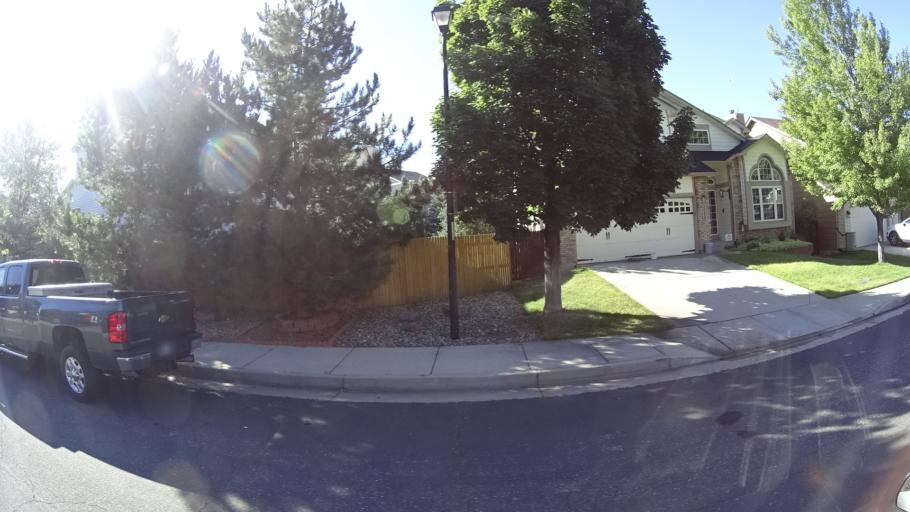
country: US
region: Colorado
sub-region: El Paso County
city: Black Forest
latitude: 38.9604
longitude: -104.7604
